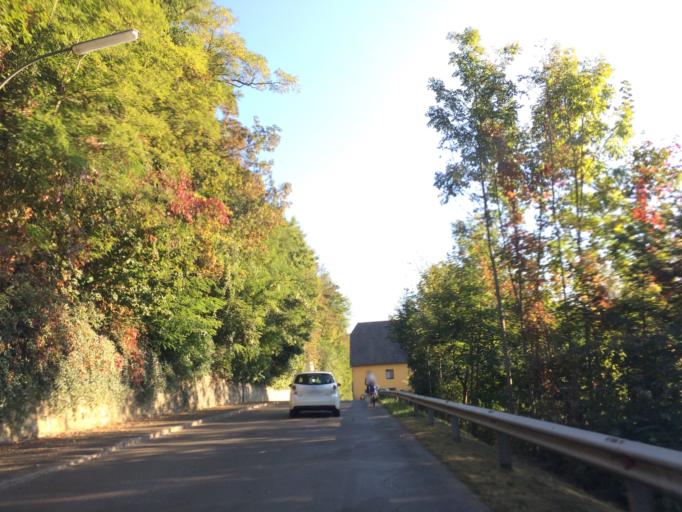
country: AT
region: Styria
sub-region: Politischer Bezirk Leoben
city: Leoben
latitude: 47.3693
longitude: 15.0979
